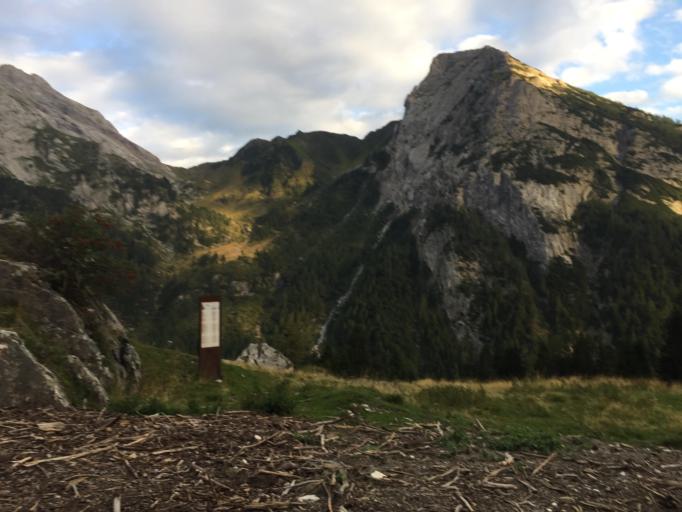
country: IT
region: Friuli Venezia Giulia
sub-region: Provincia di Udine
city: Forni Avoltri
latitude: 46.6178
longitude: 12.8074
